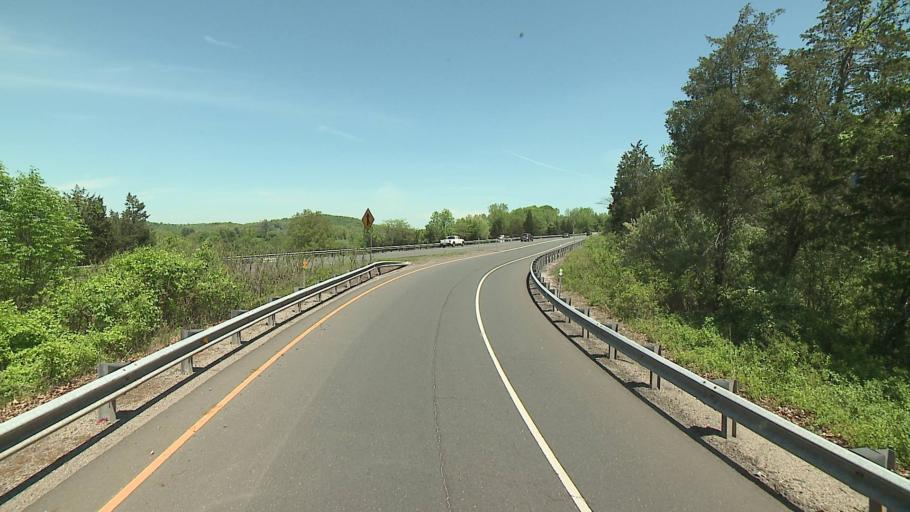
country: US
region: Connecticut
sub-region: New Haven County
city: Heritage Village
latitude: 41.4561
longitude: -73.2358
